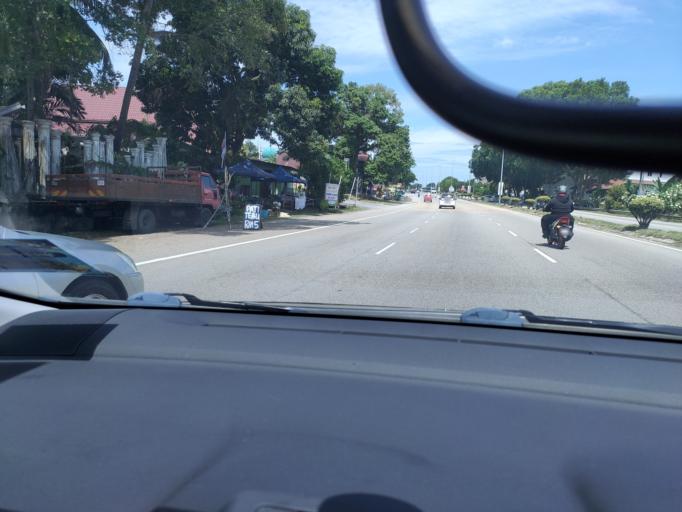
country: MY
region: Melaka
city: Batu Berendam
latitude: 2.2650
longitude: 102.2184
